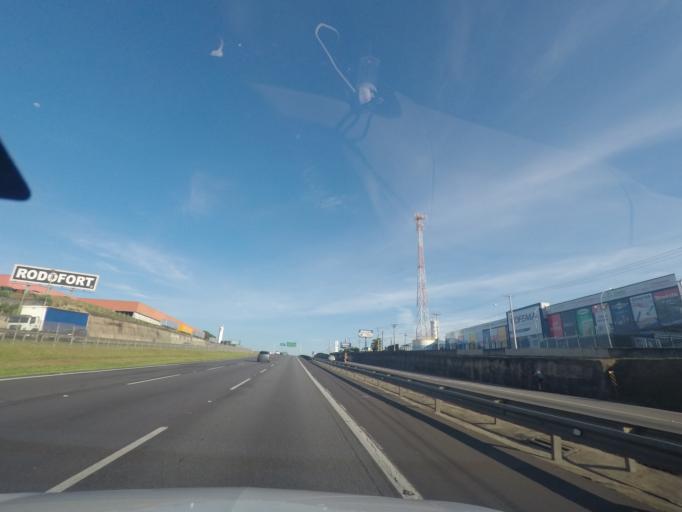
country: BR
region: Sao Paulo
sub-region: Hortolandia
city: Hortolandia
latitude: -22.8346
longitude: -47.1754
